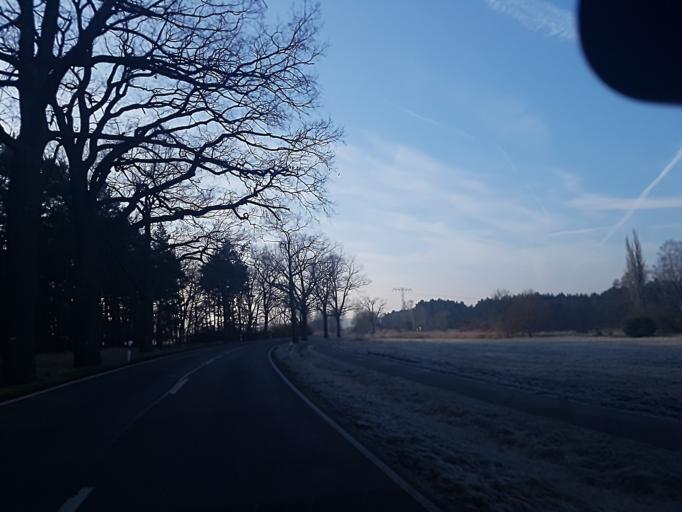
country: DE
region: Brandenburg
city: Golzow
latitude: 52.2563
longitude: 12.5986
